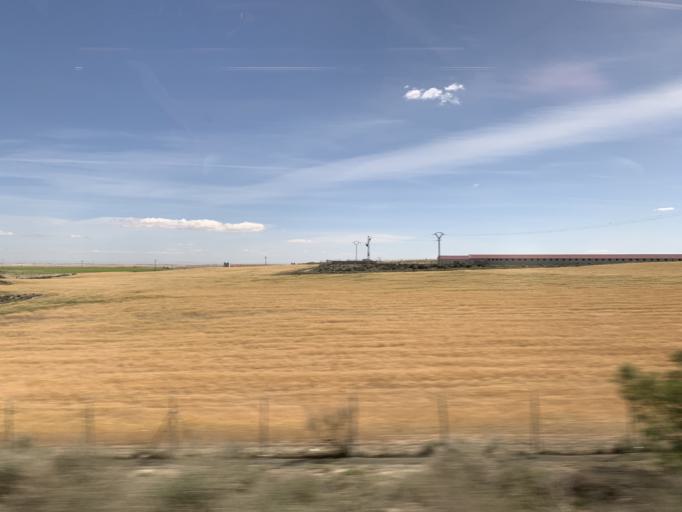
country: ES
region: Aragon
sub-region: Provincia de Zaragoza
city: Bujaraloz
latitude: 41.5263
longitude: -0.1464
